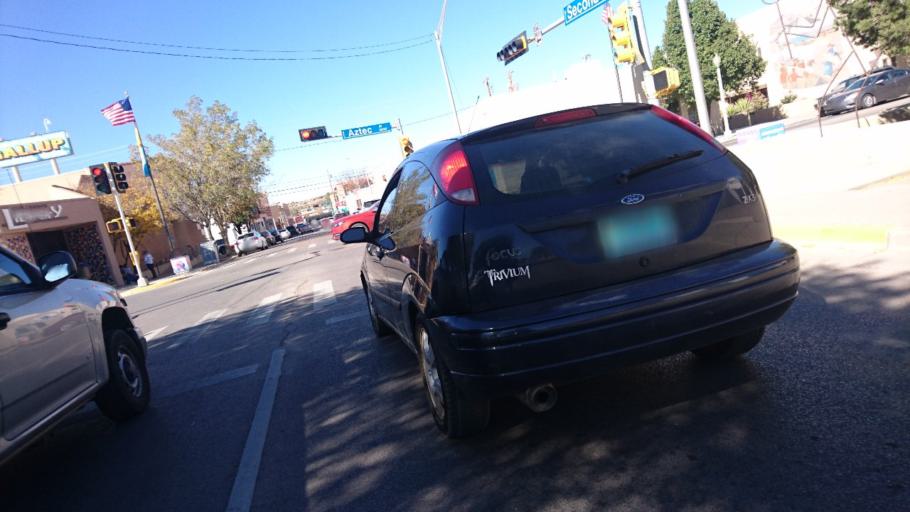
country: US
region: New Mexico
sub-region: McKinley County
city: Gallup
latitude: 35.5262
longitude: -108.7420
